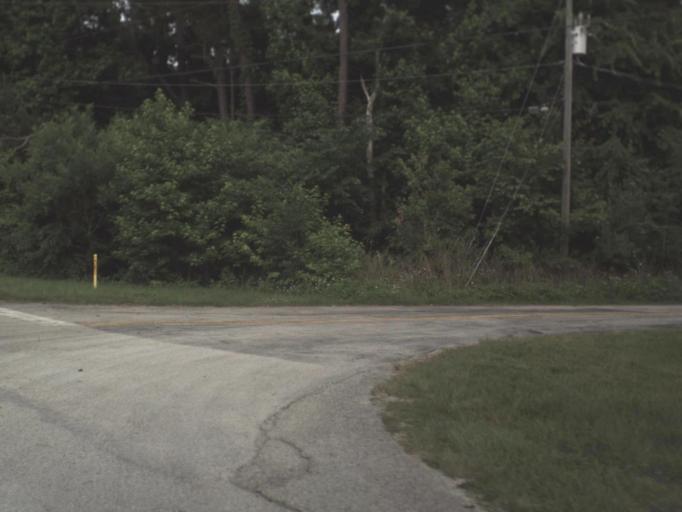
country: US
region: Florida
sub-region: Clay County
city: Green Cove Springs
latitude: 29.9918
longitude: -81.6068
